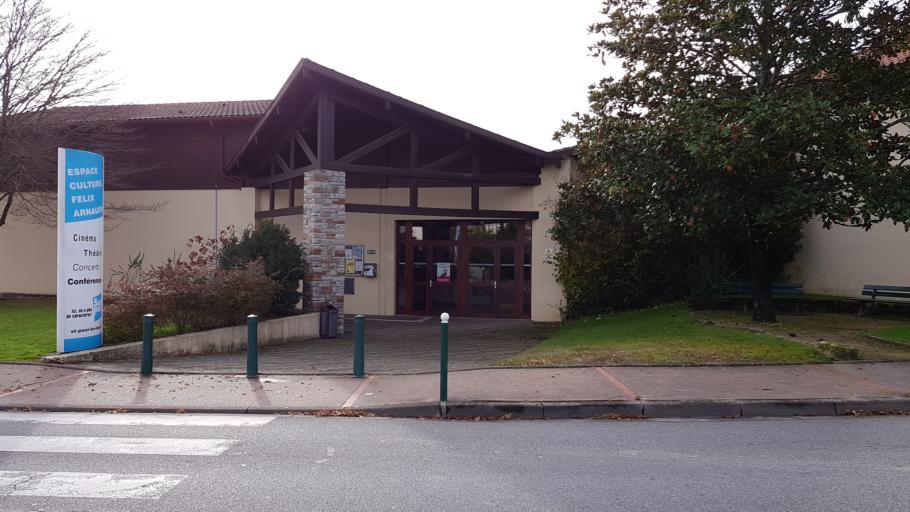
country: FR
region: Aquitaine
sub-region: Departement des Landes
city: Saint-Paul-les-Dax
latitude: 43.7233
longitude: -1.0552
